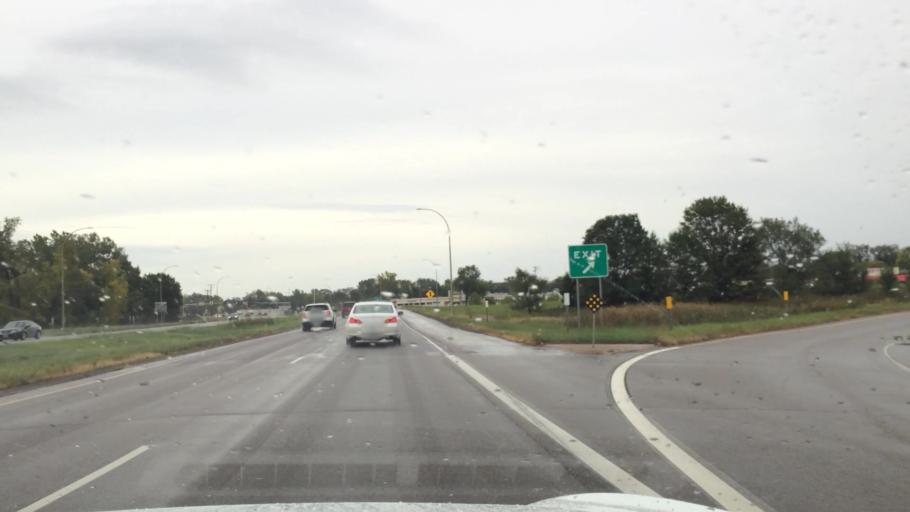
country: US
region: Minnesota
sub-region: Anoka County
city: Spring Lake Park
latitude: 45.1213
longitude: -93.2370
